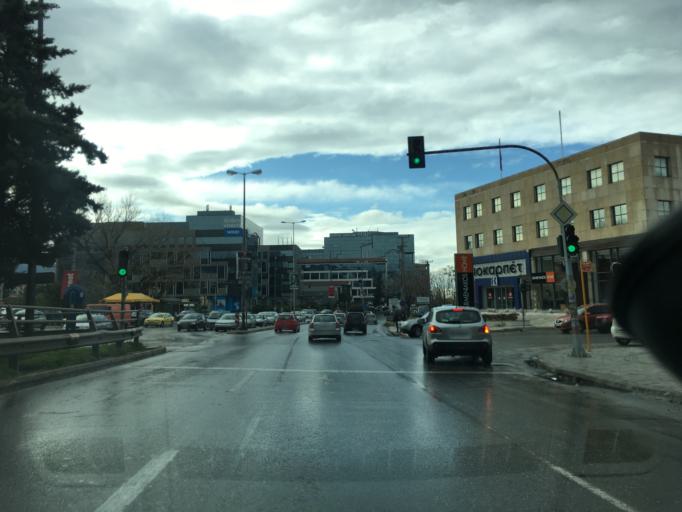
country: GR
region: Attica
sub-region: Nomarchia Athinas
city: Marousi
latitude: 38.0468
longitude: 23.8075
